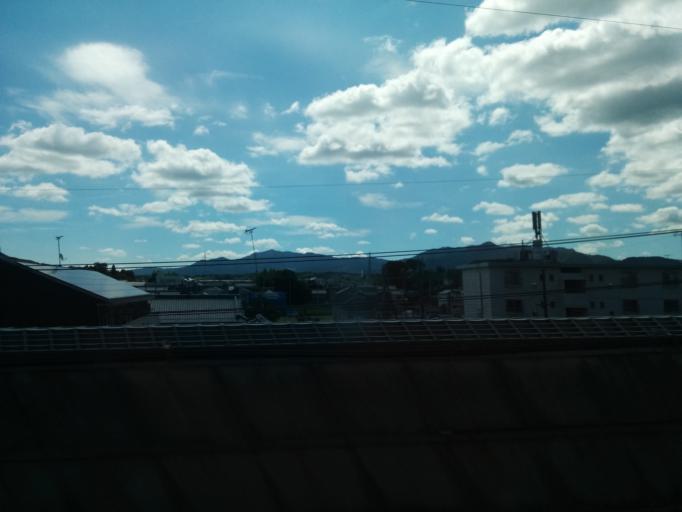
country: JP
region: Shiga Prefecture
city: Kusatsu
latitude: 35.0155
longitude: 135.9765
